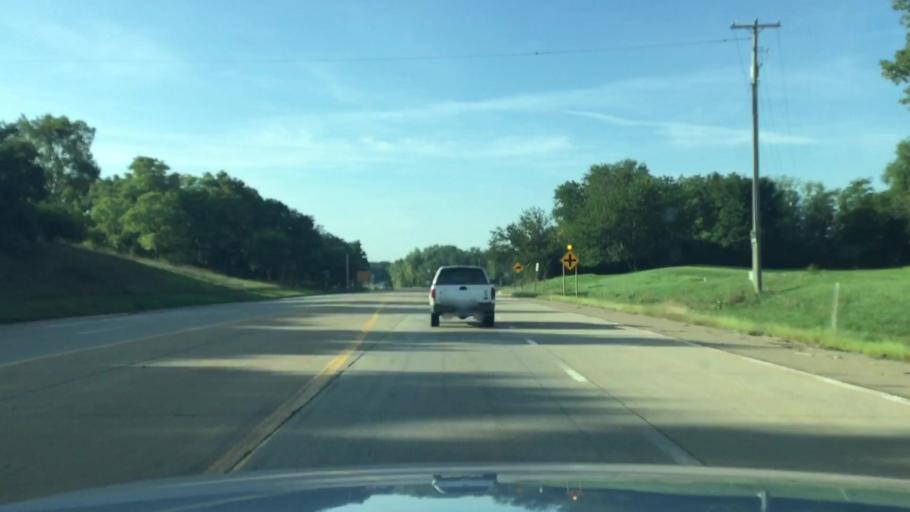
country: US
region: Michigan
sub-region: Jackson County
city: Vandercook Lake
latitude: 42.1921
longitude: -84.3697
